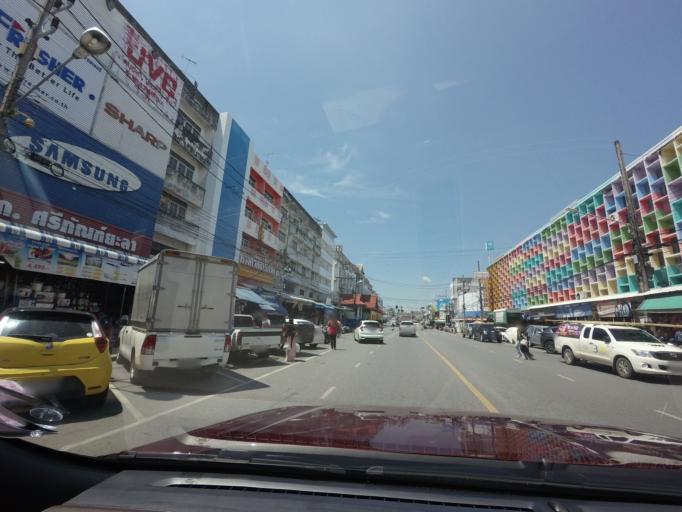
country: TH
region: Yala
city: Yala
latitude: 6.5610
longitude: 101.2922
